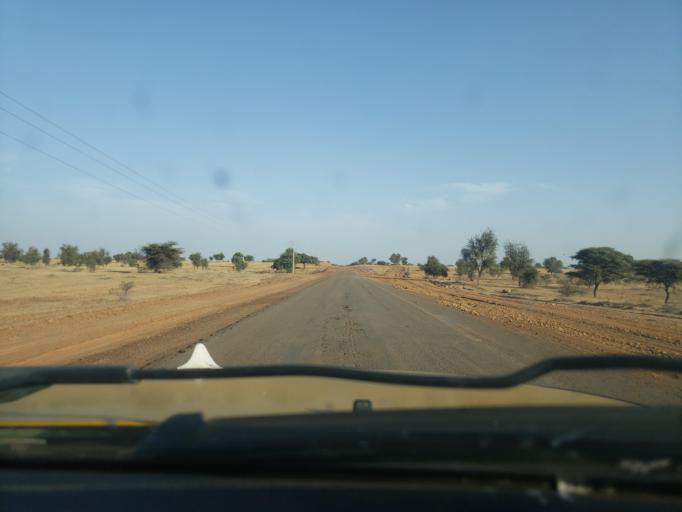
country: SN
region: Louga
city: Dara
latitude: 15.4282
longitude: -15.7448
